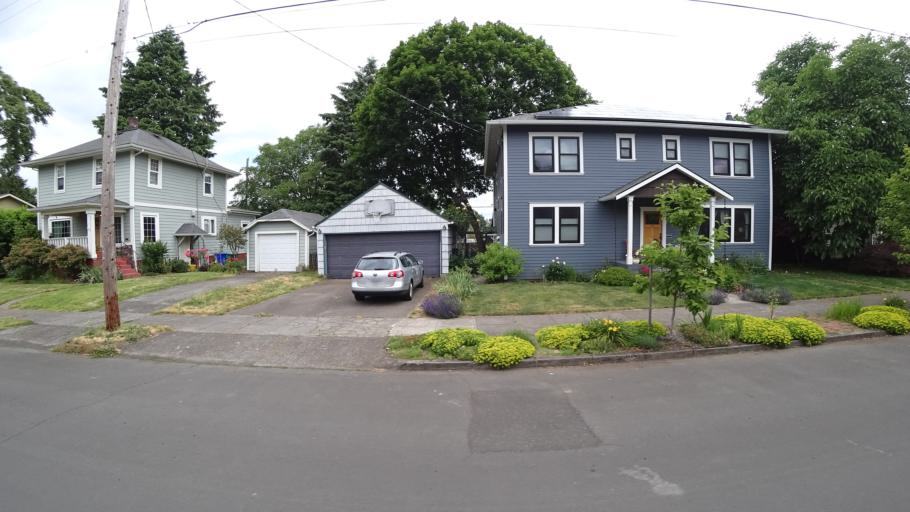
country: US
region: Oregon
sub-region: Multnomah County
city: Portland
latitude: 45.5765
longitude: -122.7202
